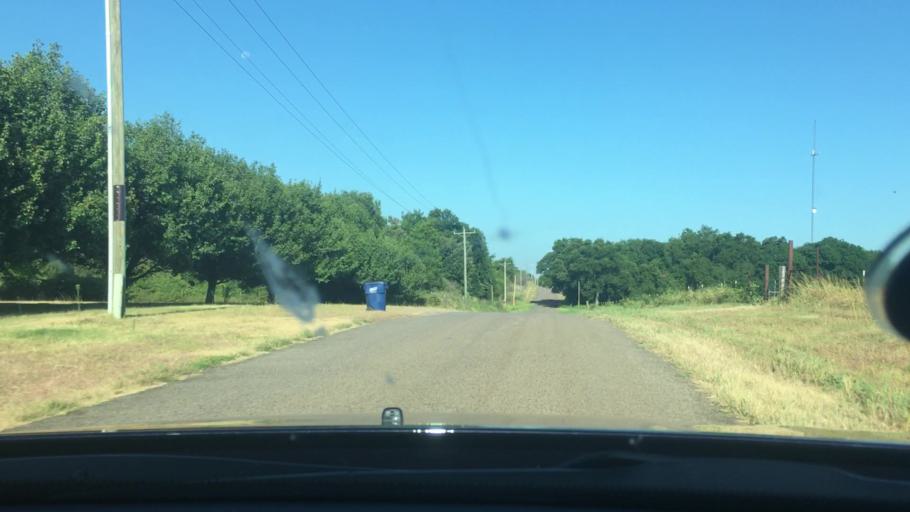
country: US
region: Oklahoma
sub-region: Murray County
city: Sulphur
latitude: 34.4049
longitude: -96.8131
